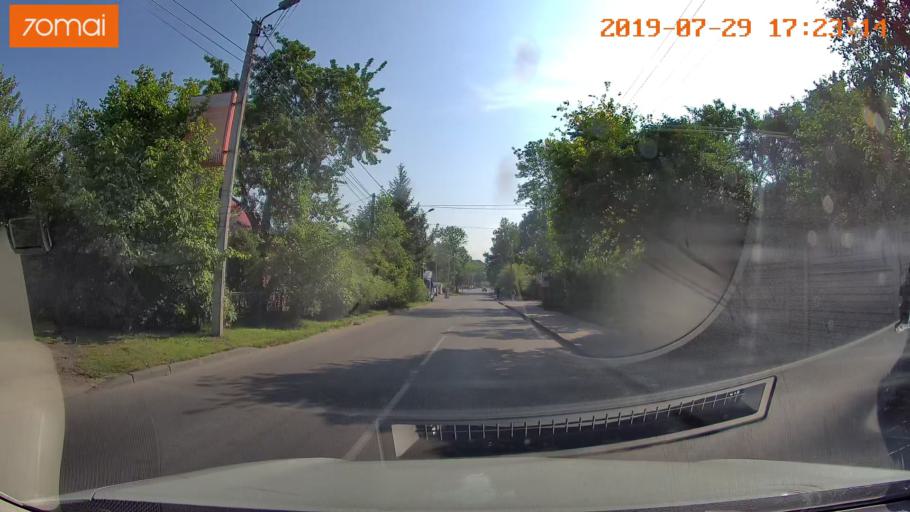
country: RU
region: Kaliningrad
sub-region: Gorod Kaliningrad
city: Kaliningrad
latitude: 54.7678
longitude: 20.4474
